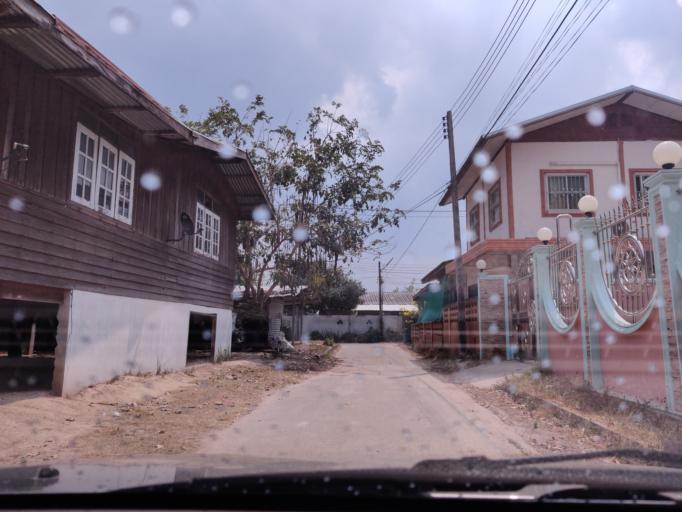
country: TH
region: Sisaket
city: Si Sa Ket
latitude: 15.1027
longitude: 104.3541
